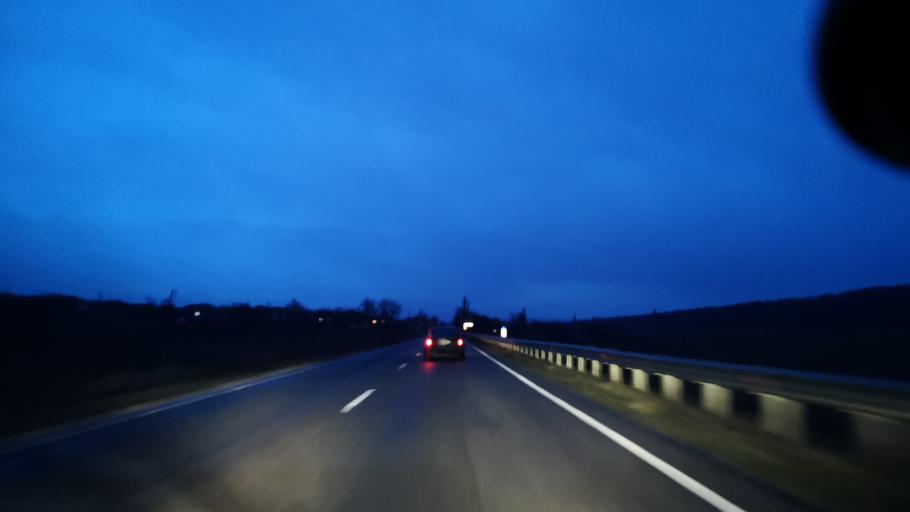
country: MD
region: Orhei
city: Orhei
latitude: 47.4194
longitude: 28.8081
